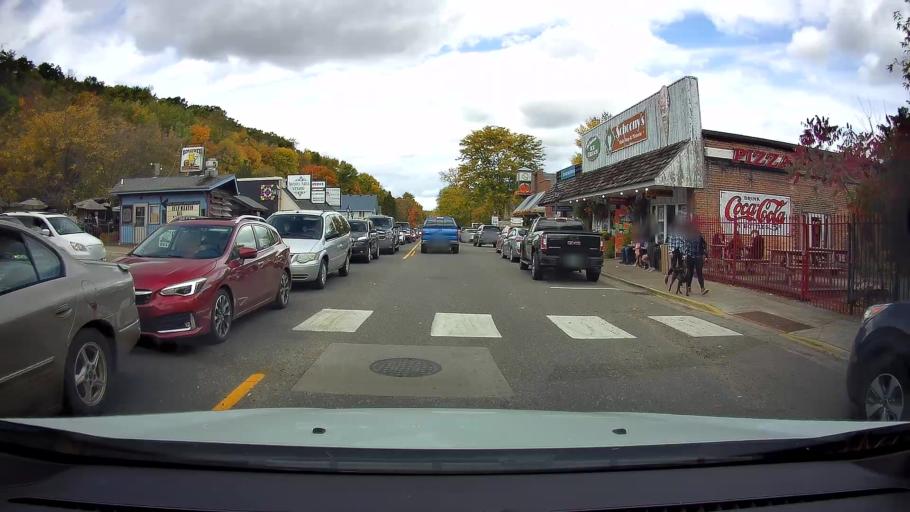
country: US
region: Wisconsin
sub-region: Polk County
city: Saint Croix Falls
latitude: 45.4023
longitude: -92.6526
